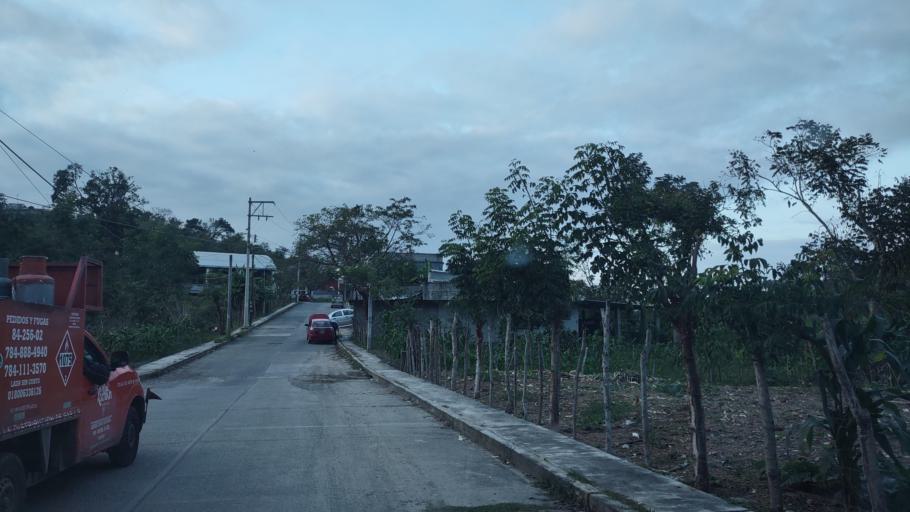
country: MX
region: Veracruz
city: Papantla de Olarte
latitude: 20.4578
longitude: -97.3066
